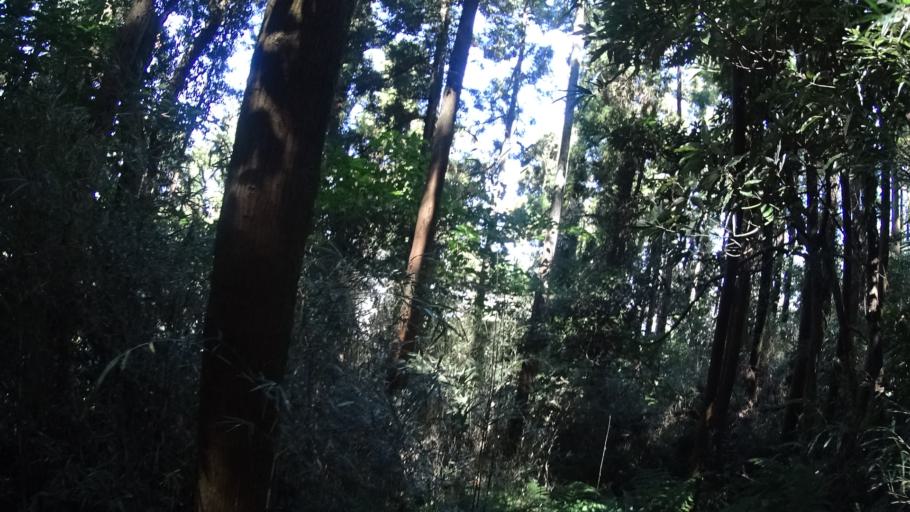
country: JP
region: Kanagawa
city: Hayama
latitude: 35.2786
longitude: 139.5914
